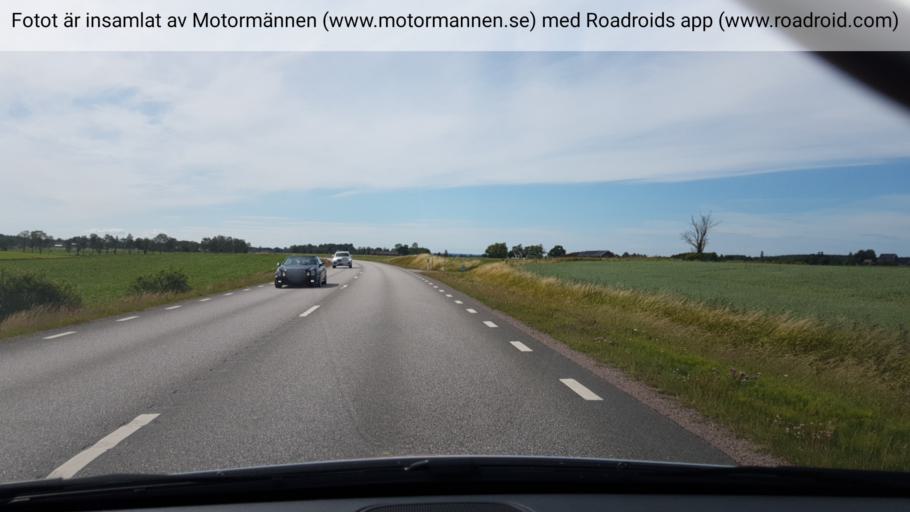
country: SE
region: Vaestra Goetaland
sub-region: Tibro Kommun
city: Tibro
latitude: 58.3512
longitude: 14.0836
